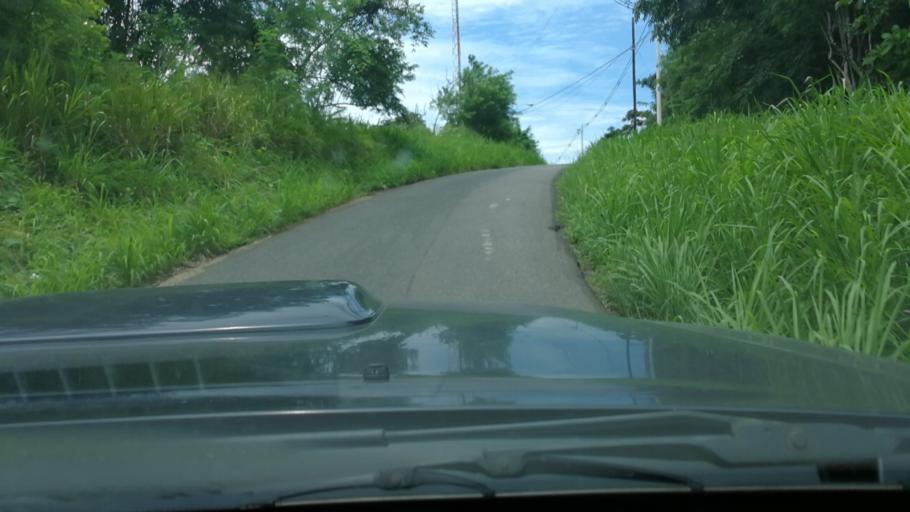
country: PA
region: Panama
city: San Miguelito
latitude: 9.1032
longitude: -79.4558
